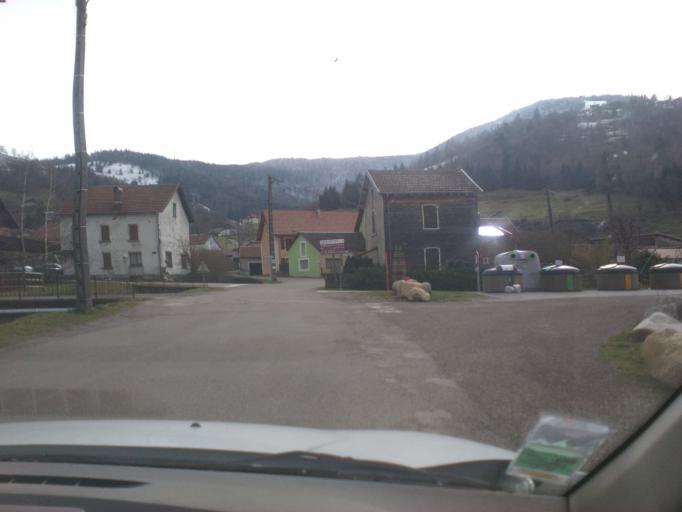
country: FR
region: Lorraine
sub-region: Departement des Vosges
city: Bussang
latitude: 47.8837
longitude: 6.8543
